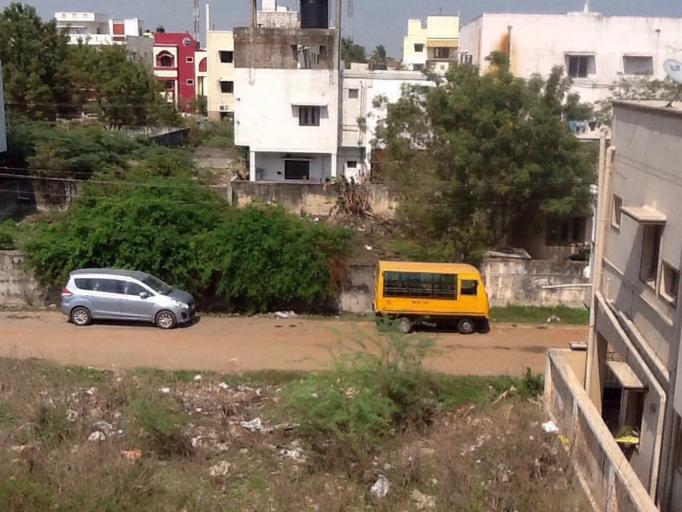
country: IN
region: Tamil Nadu
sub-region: Thiruvallur
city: Porur
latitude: 13.0615
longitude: 80.1690
